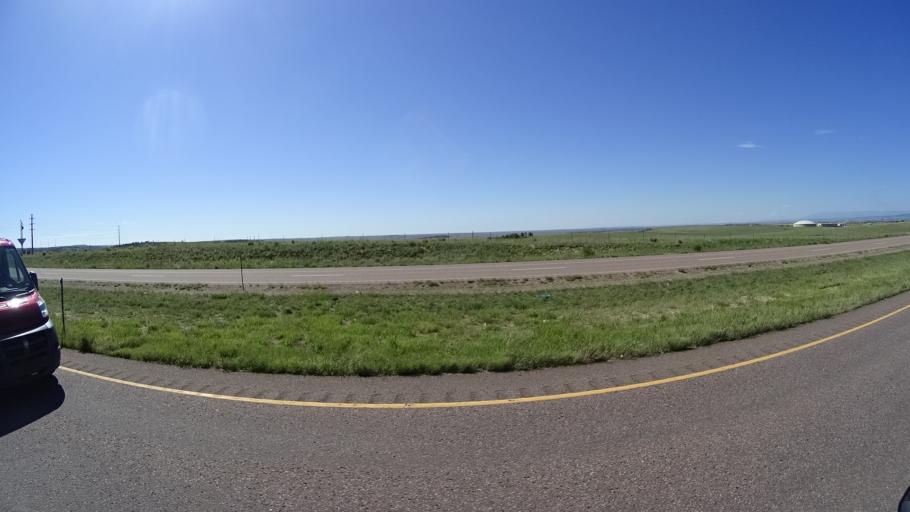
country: US
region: Colorado
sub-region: El Paso County
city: Cimarron Hills
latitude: 38.8570
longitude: -104.6754
